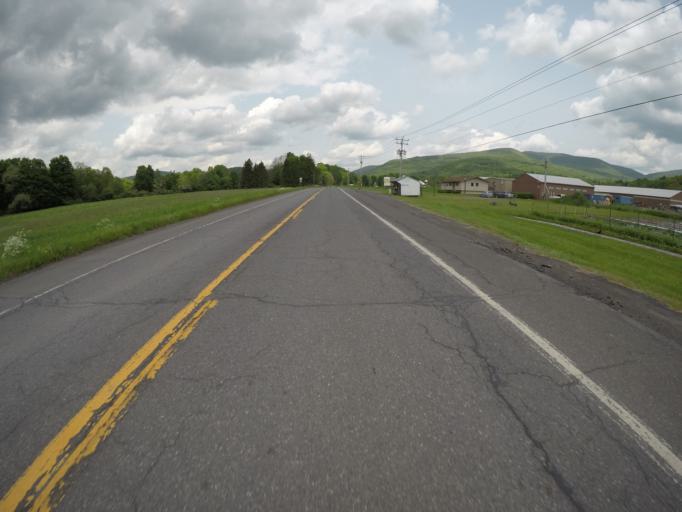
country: US
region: New York
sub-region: Delaware County
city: Stamford
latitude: 42.2951
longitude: -74.5587
